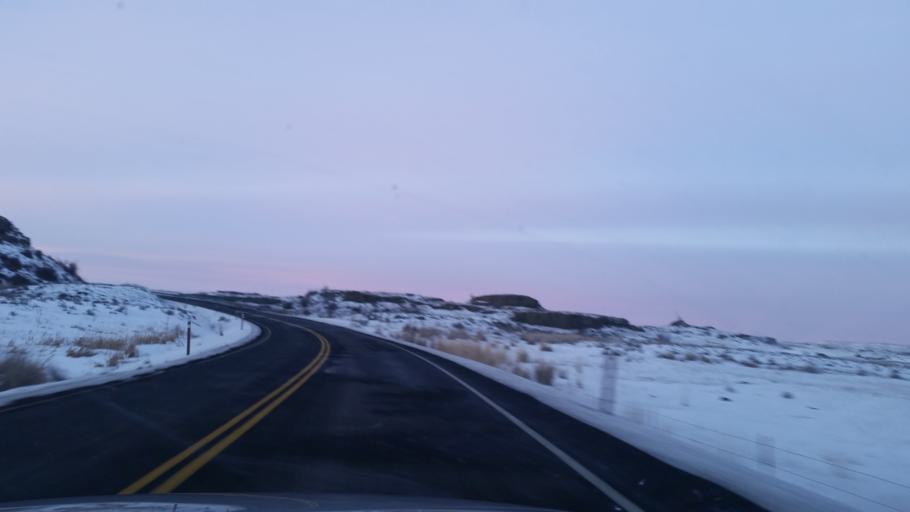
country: US
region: Washington
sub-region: Spokane County
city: Medical Lake
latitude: 47.2621
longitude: -117.9283
